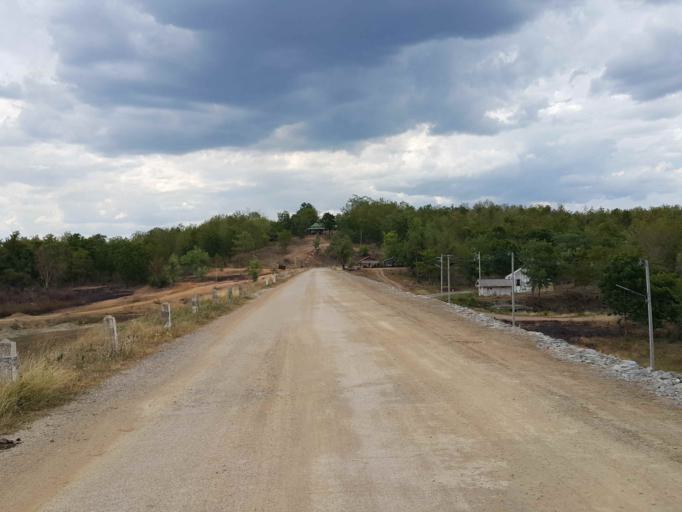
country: TH
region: Sukhothai
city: Thung Saliam
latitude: 17.3254
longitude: 99.4222
